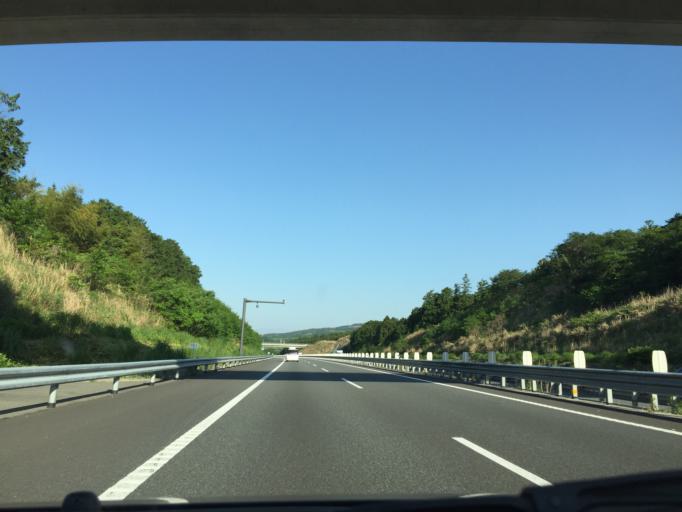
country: JP
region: Shizuoka
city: Numazu
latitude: 35.1535
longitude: 138.8370
